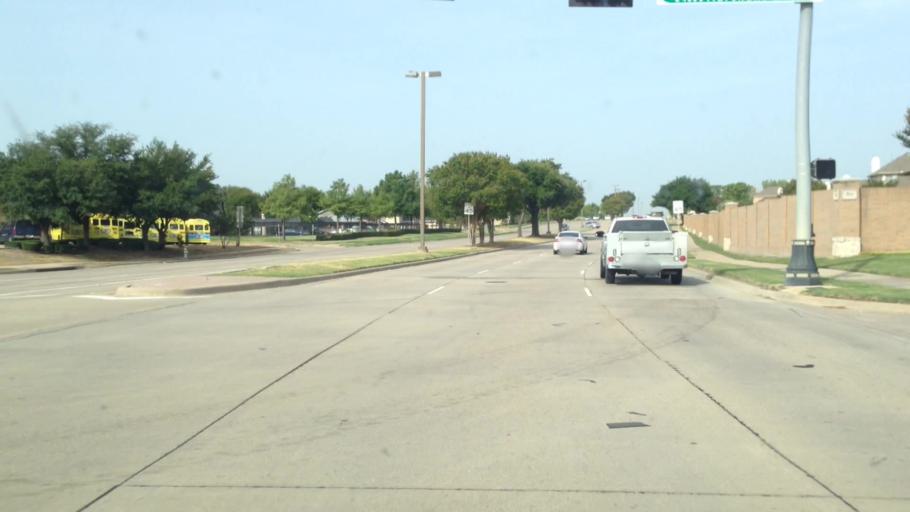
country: US
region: Texas
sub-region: Denton County
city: Lewisville
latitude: 33.0151
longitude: -96.9462
